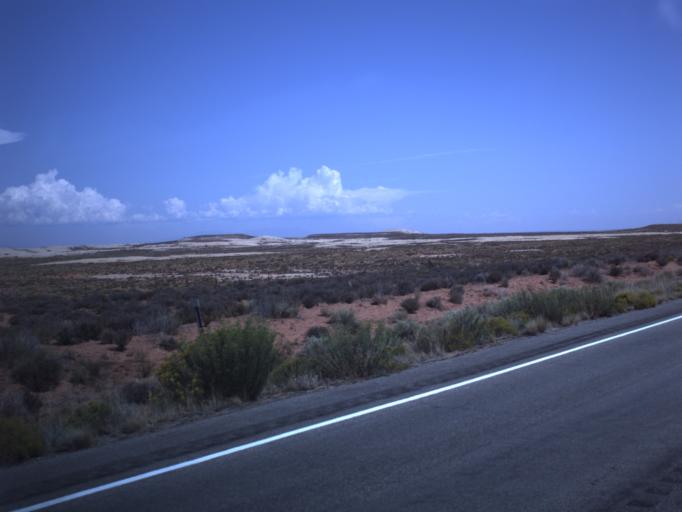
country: US
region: Utah
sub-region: San Juan County
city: Blanding
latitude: 37.0297
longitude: -109.5966
